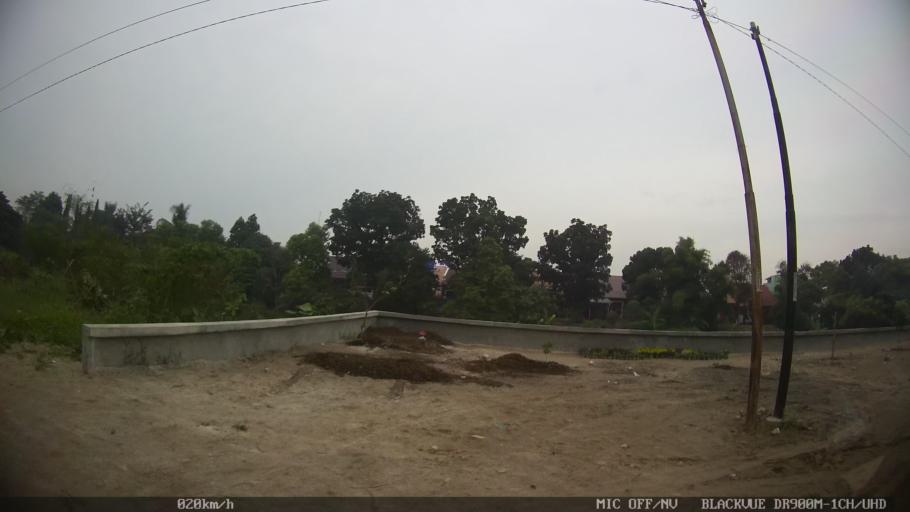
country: ID
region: North Sumatra
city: Deli Tua
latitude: 3.5437
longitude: 98.7145
